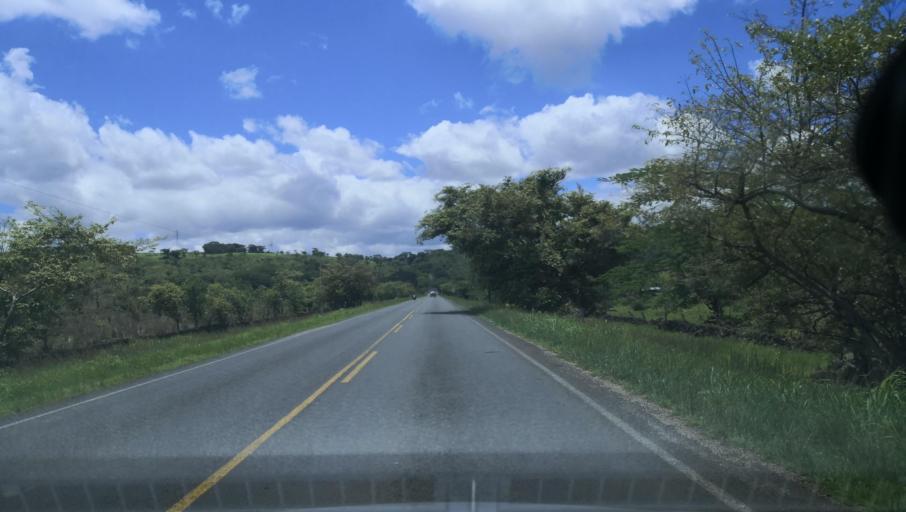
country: NI
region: Esteli
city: Esteli
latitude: 13.2015
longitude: -86.3750
